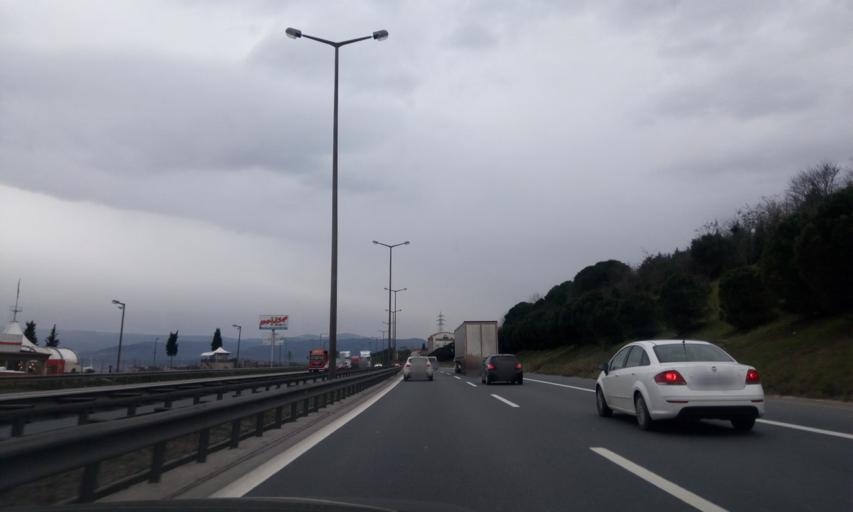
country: TR
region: Kocaeli
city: Izmit
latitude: 40.7752
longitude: 29.8737
